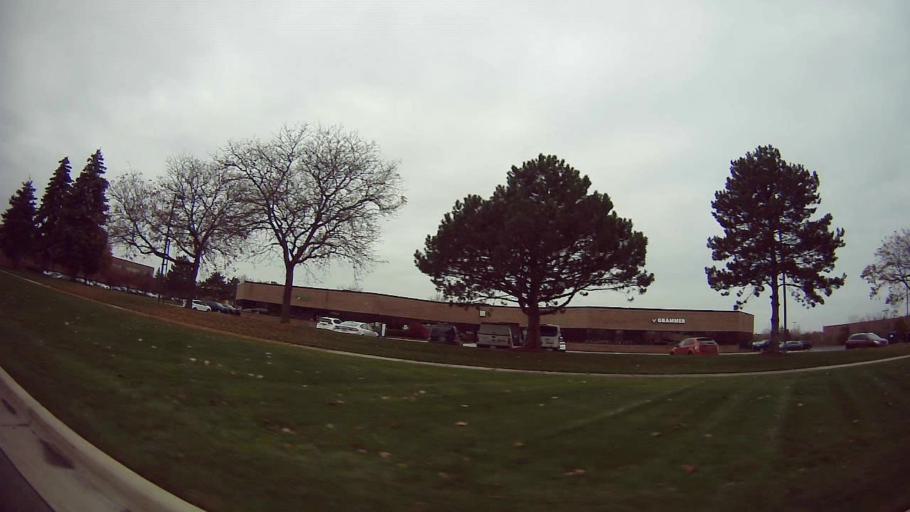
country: US
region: Michigan
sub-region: Oakland County
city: Clawson
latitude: 42.5447
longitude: -83.1076
